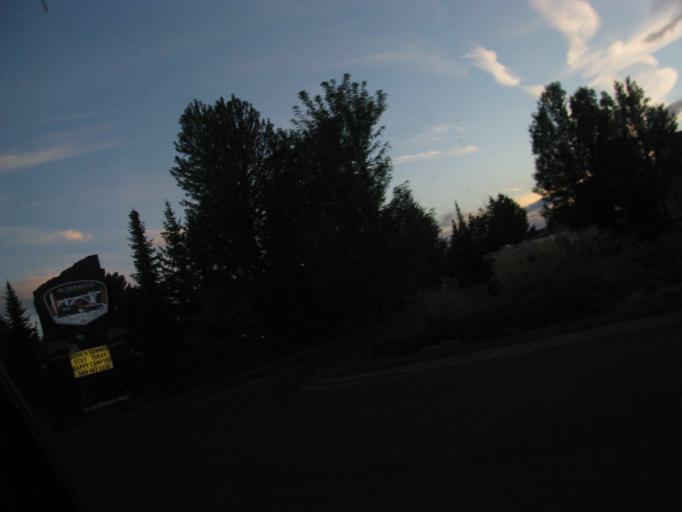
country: US
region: Washington
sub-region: Spokane County
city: Mead
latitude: 47.7858
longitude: -117.3537
